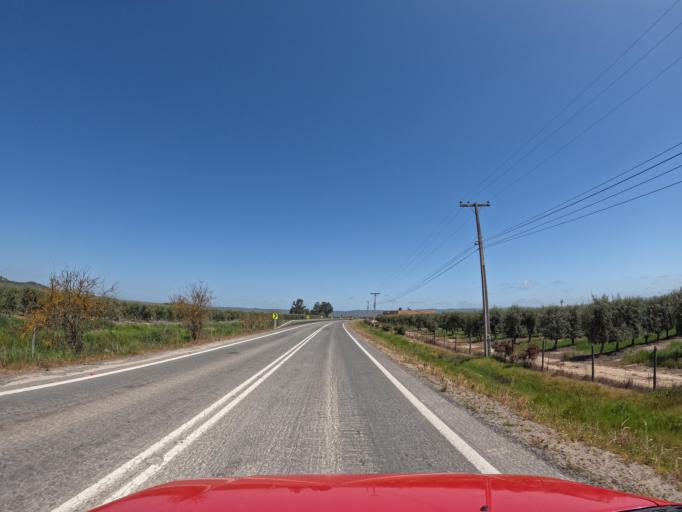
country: CL
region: O'Higgins
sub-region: Provincia de Colchagua
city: Santa Cruz
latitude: -34.7356
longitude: -71.7030
